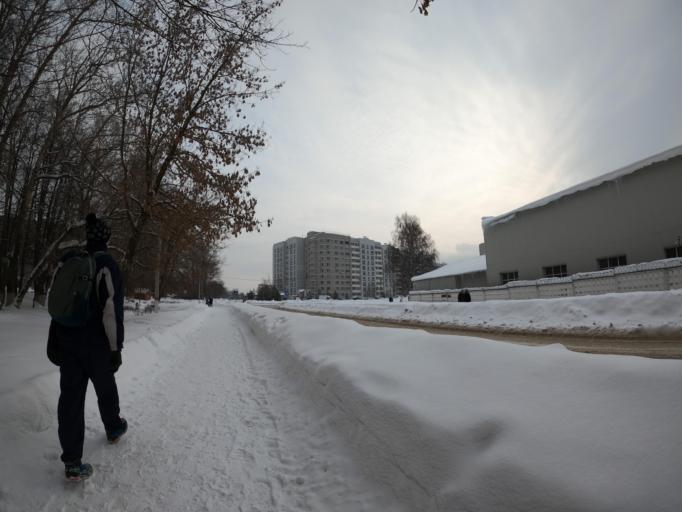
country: RU
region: Moskovskaya
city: Elektrogorsk
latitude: 55.8883
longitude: 38.7736
